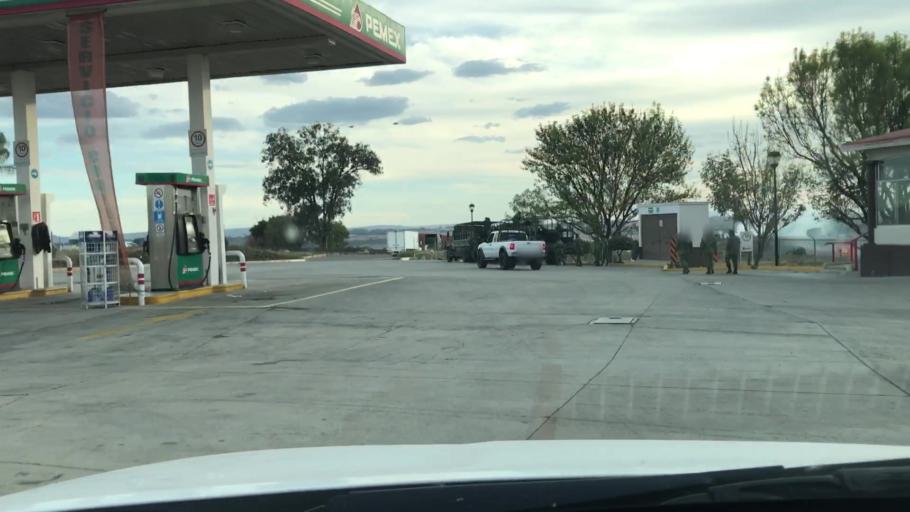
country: MX
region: Jalisco
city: Tepatitlan de Morelos
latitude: 20.8155
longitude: -102.8025
